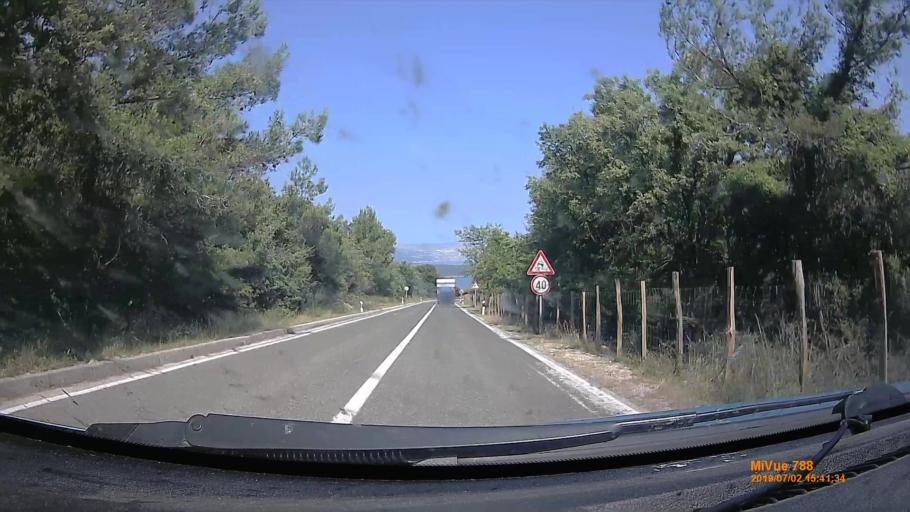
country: HR
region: Primorsko-Goranska
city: Cres
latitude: 44.9609
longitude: 14.4441
